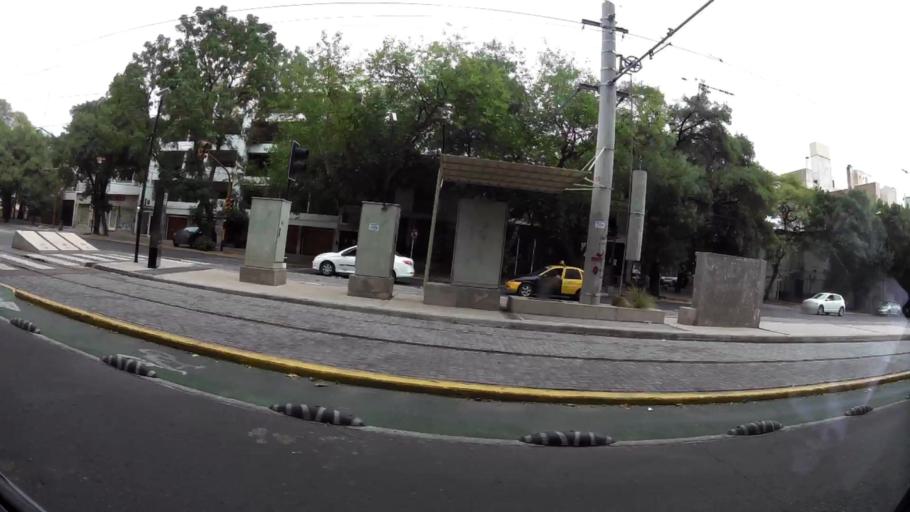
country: AR
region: Mendoza
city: Mendoza
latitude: -32.8895
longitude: -68.8498
